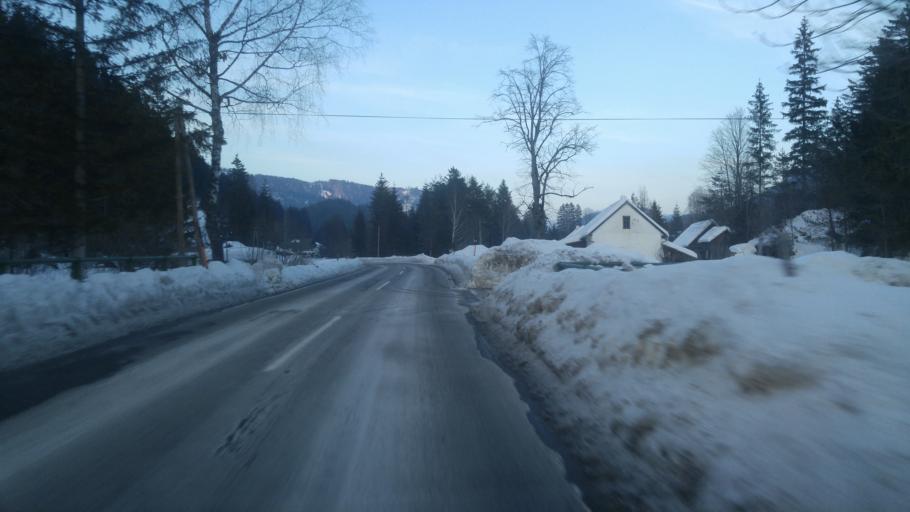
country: AT
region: Lower Austria
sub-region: Politischer Bezirk Wiener Neustadt
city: Rohr im Gebirge
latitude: 47.8767
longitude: 15.7058
